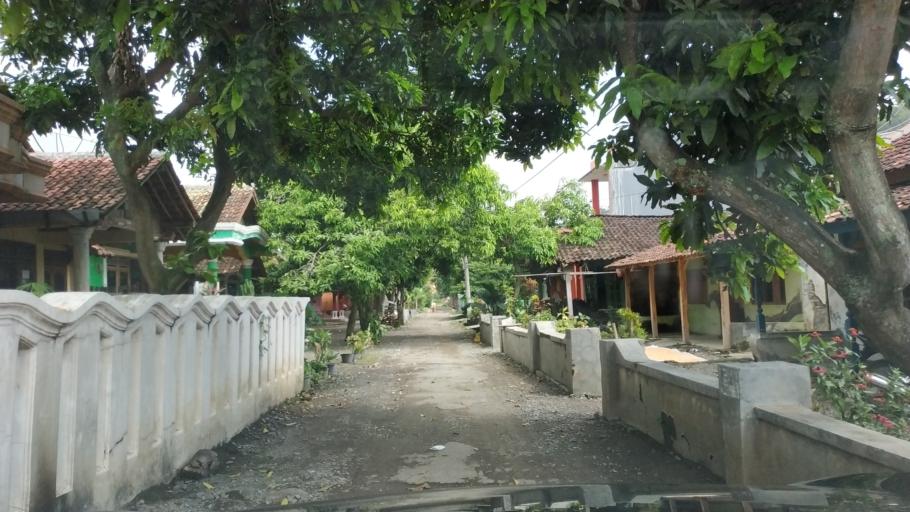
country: ID
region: Central Java
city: Margasari
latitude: -7.0930
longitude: 108.9774
